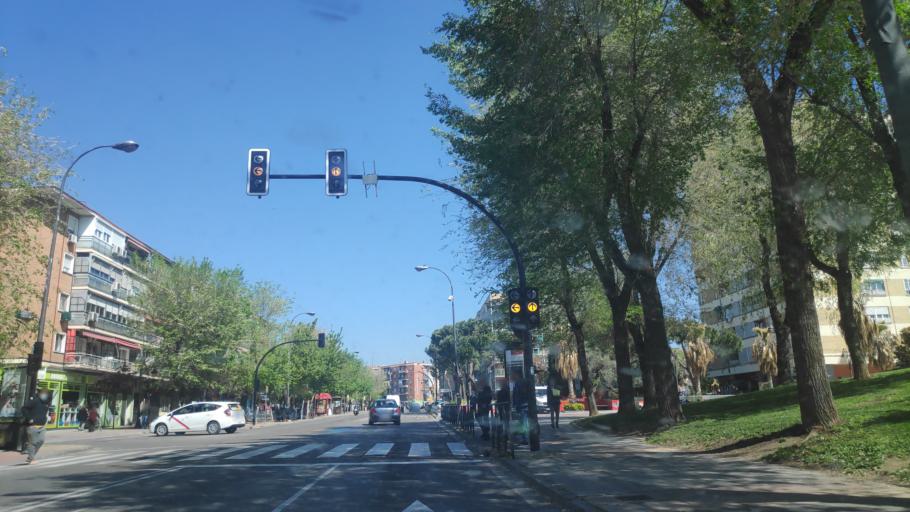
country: ES
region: Madrid
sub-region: Provincia de Madrid
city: Getafe
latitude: 40.3086
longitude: -3.7250
